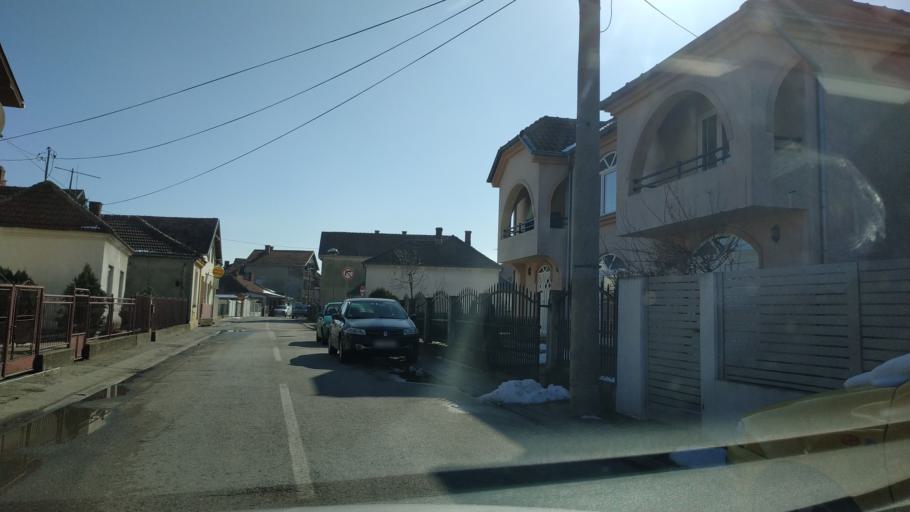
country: RS
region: Central Serbia
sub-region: Nisavski Okrug
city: Aleksinac
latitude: 43.5453
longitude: 21.7090
